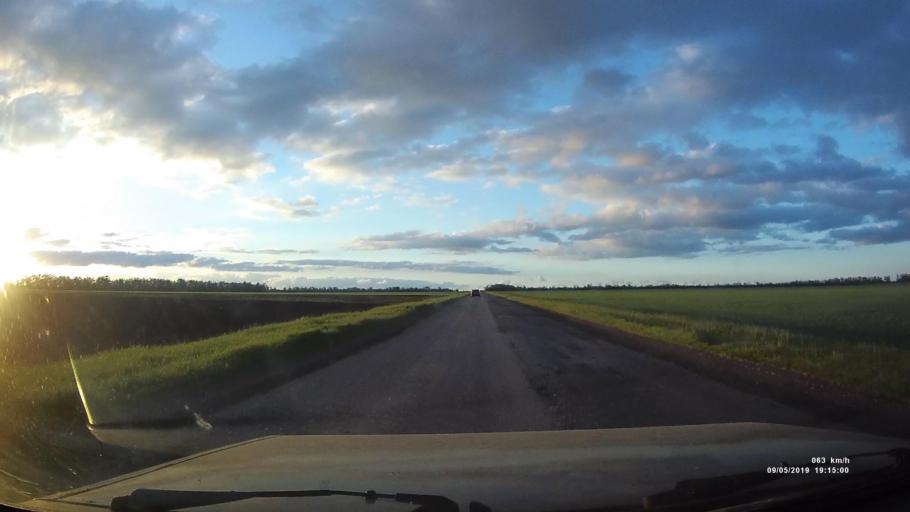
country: RU
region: Krasnodarskiy
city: Kanelovskaya
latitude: 46.7636
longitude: 39.2120
